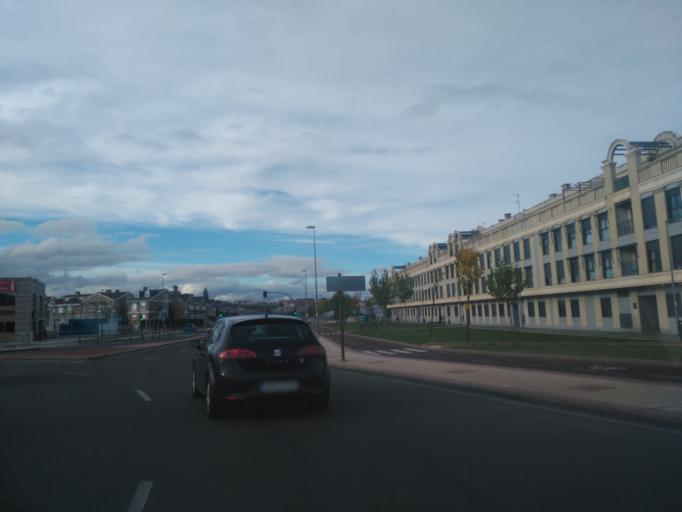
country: ES
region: Castille and Leon
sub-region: Provincia de Salamanca
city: Santa Marta de Tormes
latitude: 40.9509
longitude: -5.6400
